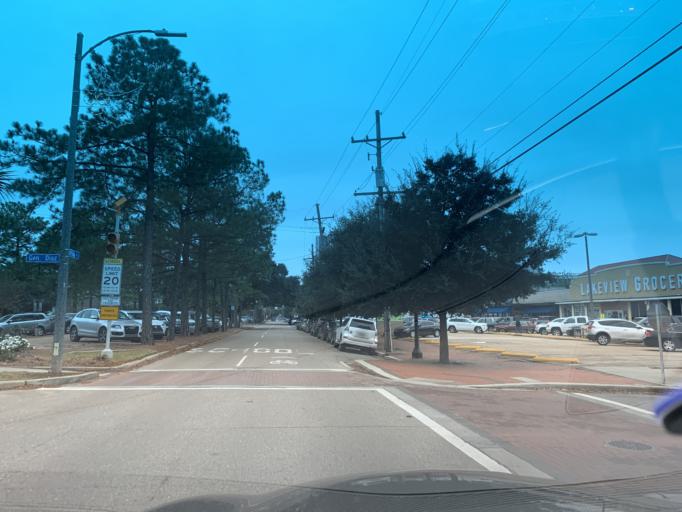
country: US
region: Louisiana
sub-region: Jefferson Parish
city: Metairie
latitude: 30.0045
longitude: -90.1047
